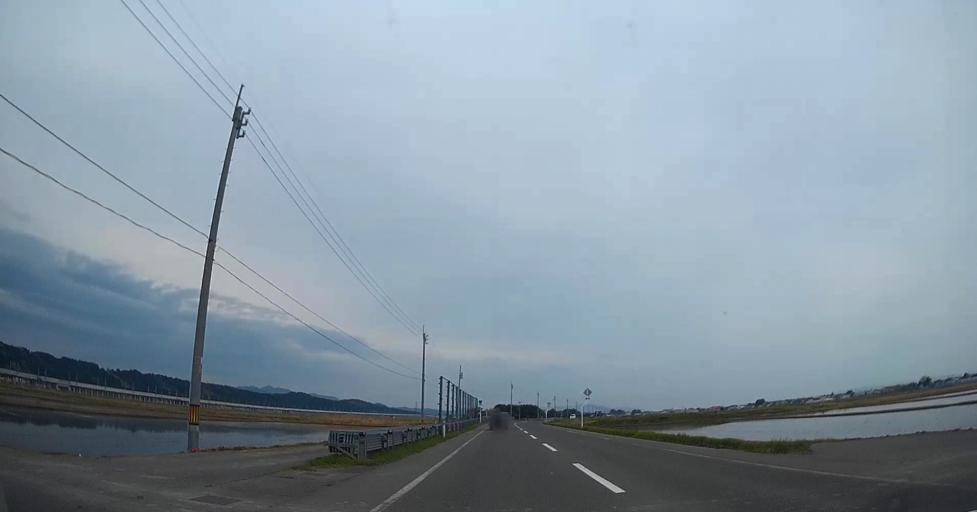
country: JP
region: Aomori
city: Aomori Shi
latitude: 40.8777
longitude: 140.6714
